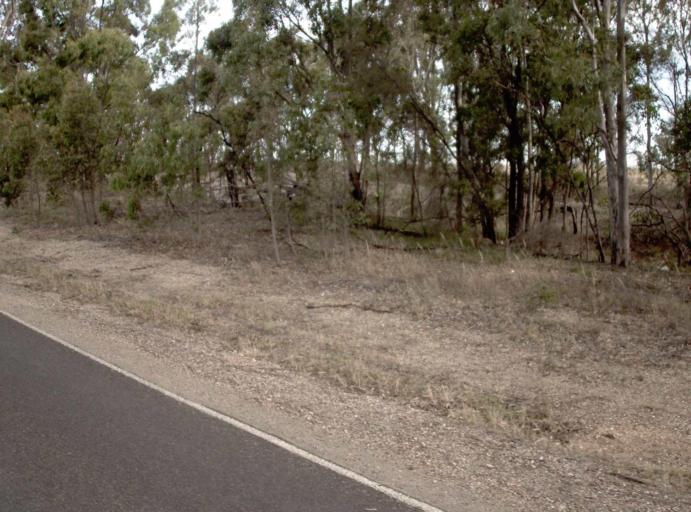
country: AU
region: Victoria
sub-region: Wellington
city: Heyfield
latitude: -37.9809
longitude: 146.8034
